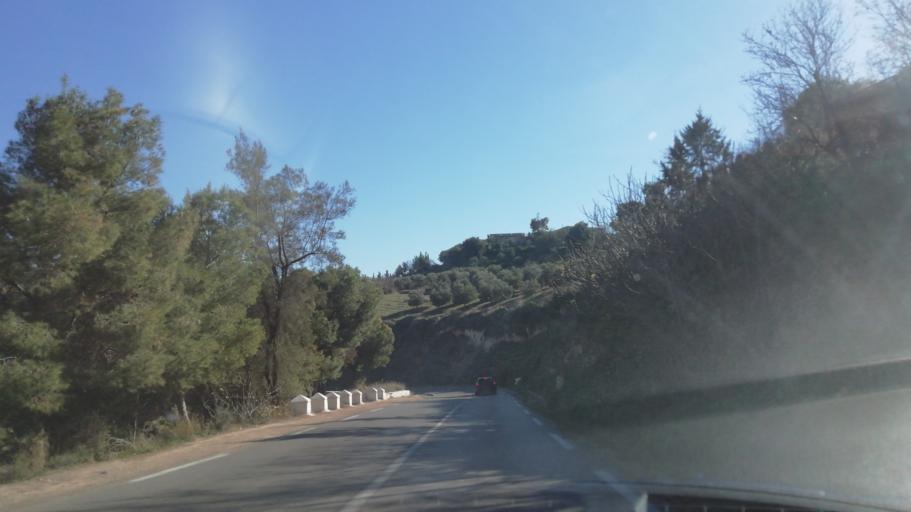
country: DZ
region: Tlemcen
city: Beni Mester
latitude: 34.8416
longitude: -1.4706
